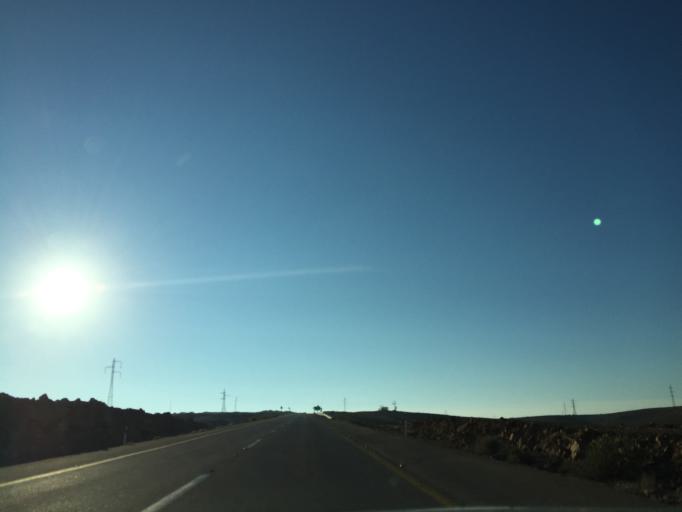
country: IL
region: Southern District
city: Mitzpe Ramon
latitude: 30.5220
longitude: 34.9385
